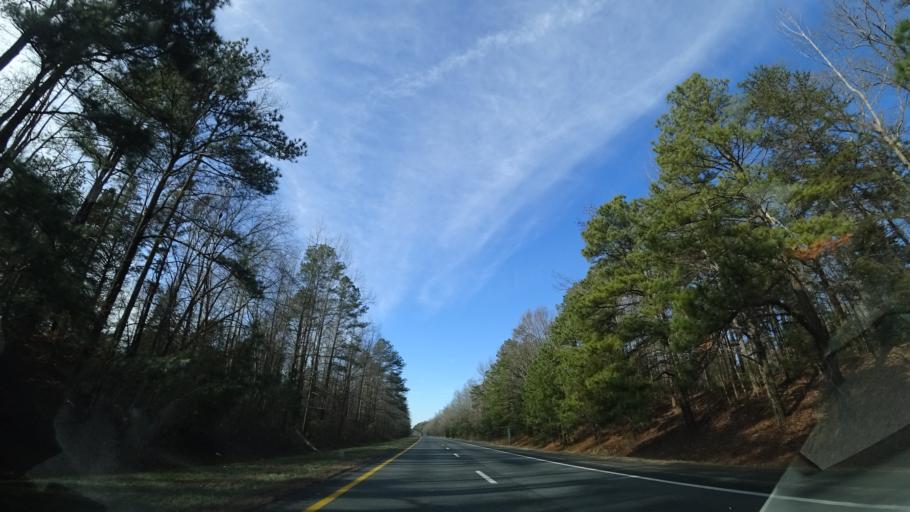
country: US
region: Virginia
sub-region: New Kent County
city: New Kent
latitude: 37.5072
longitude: -77.1080
